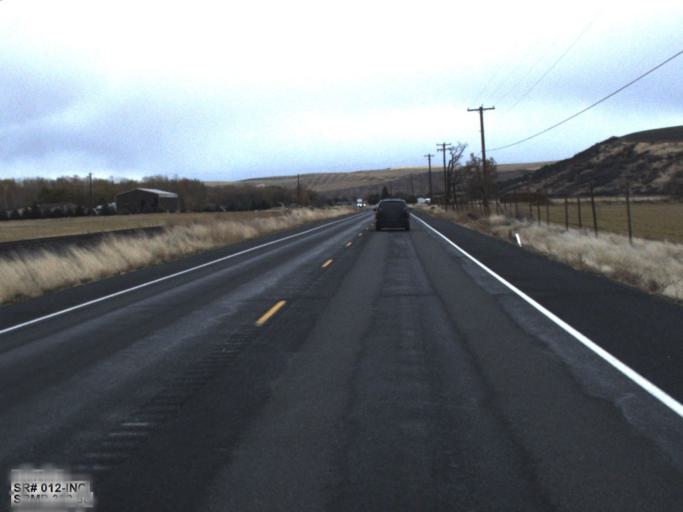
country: US
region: Washington
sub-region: Columbia County
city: Dayton
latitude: 46.2870
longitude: -118.0572
